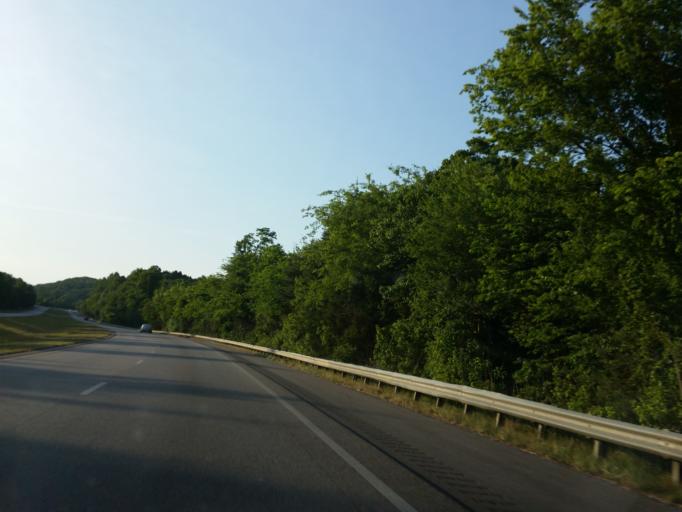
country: US
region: Georgia
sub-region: Dade County
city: Trenton
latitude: 34.7843
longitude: -85.5417
